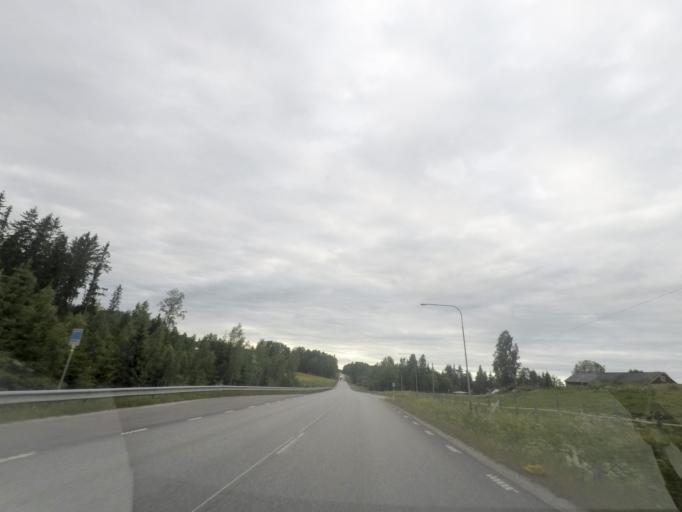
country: SE
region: OErebro
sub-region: Lindesbergs Kommun
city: Stora
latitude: 59.6772
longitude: 15.0998
